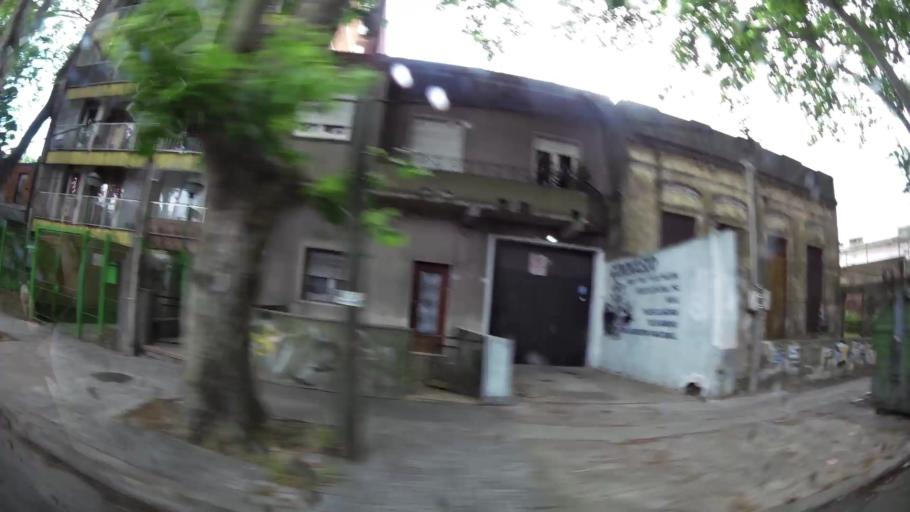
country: UY
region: Montevideo
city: Montevideo
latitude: -34.8592
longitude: -56.1771
